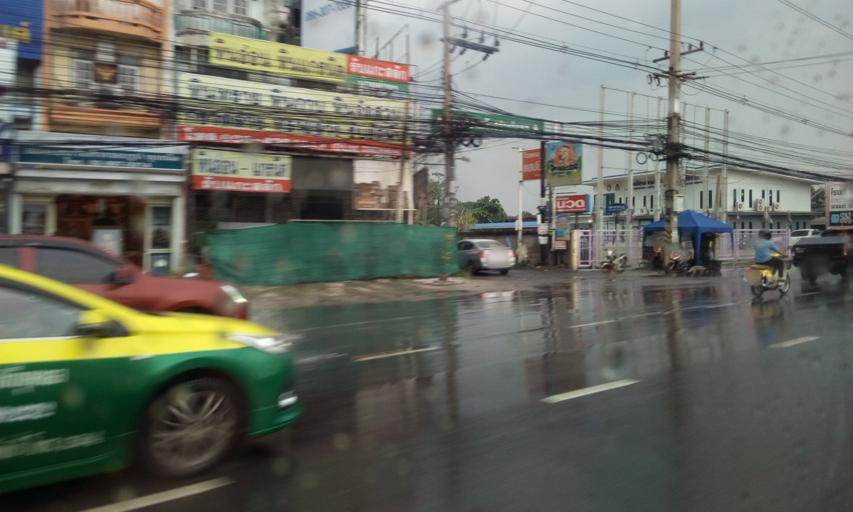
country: TH
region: Bangkok
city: Sai Mai
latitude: 13.9885
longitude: 100.6305
